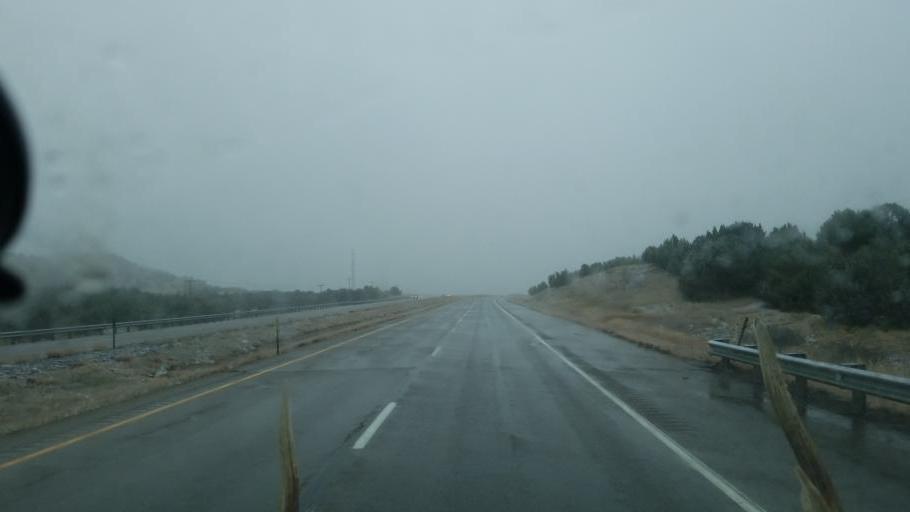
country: US
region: Colorado
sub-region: Pueblo County
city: Colorado City
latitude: 38.0358
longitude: -104.7298
